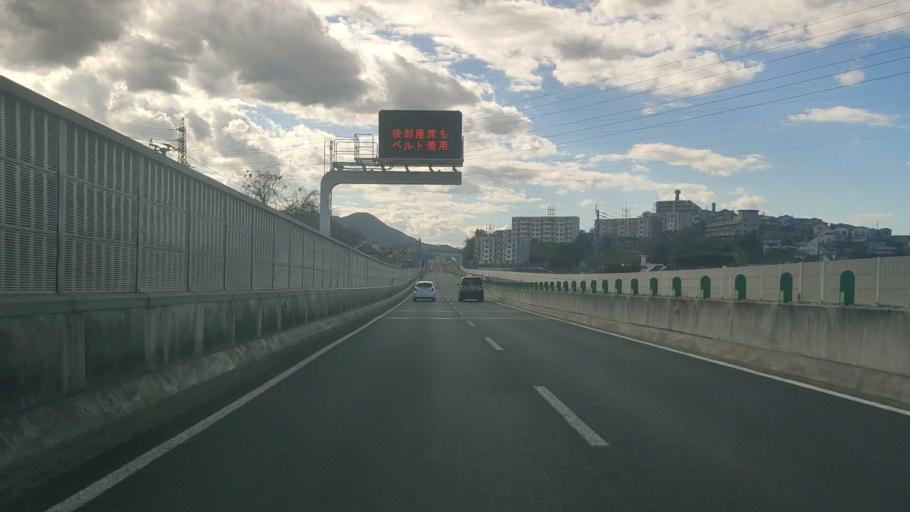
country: JP
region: Yamaguchi
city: Shimonoseki
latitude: 33.9087
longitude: 130.9539
